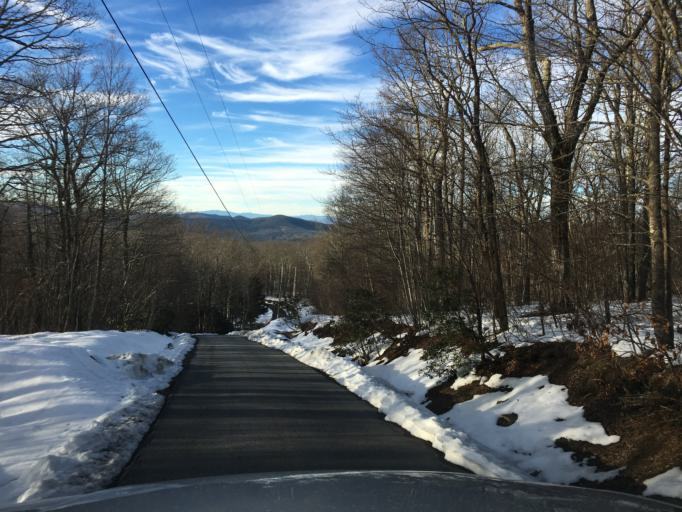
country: US
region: North Carolina
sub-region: Jackson County
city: Cullowhee
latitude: 35.1339
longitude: -82.9899
